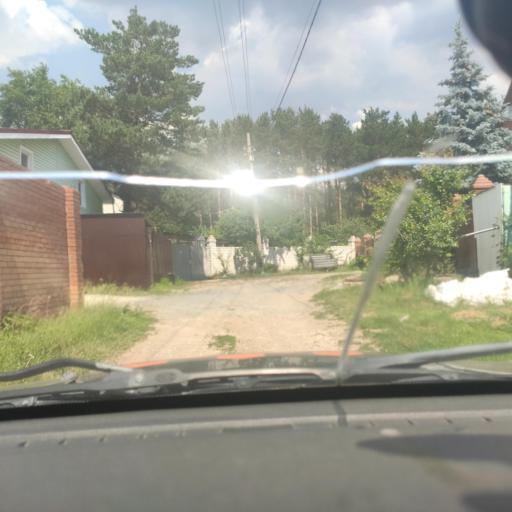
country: RU
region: Samara
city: Zhigulevsk
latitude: 53.5021
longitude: 49.5001
